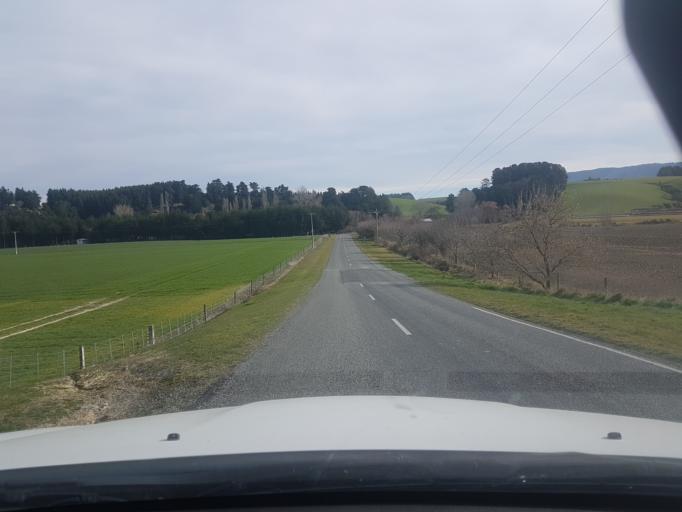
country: NZ
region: Canterbury
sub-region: Timaru District
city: Pleasant Point
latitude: -44.1292
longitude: 171.1859
